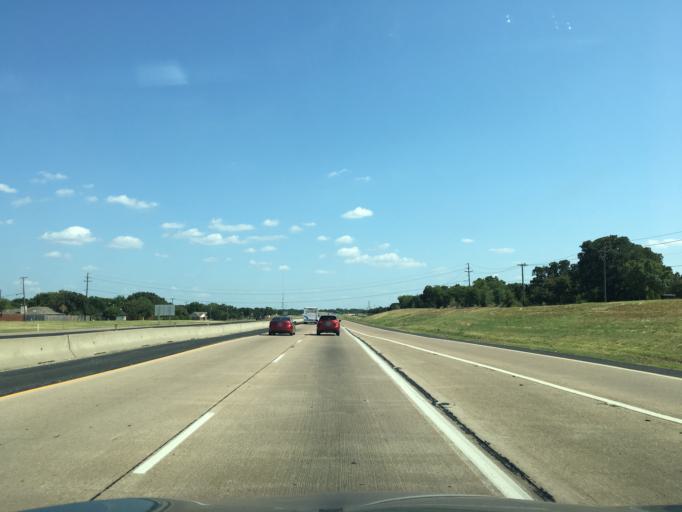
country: US
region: Texas
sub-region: Tarrant County
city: Kennedale
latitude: 32.6434
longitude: -97.1834
